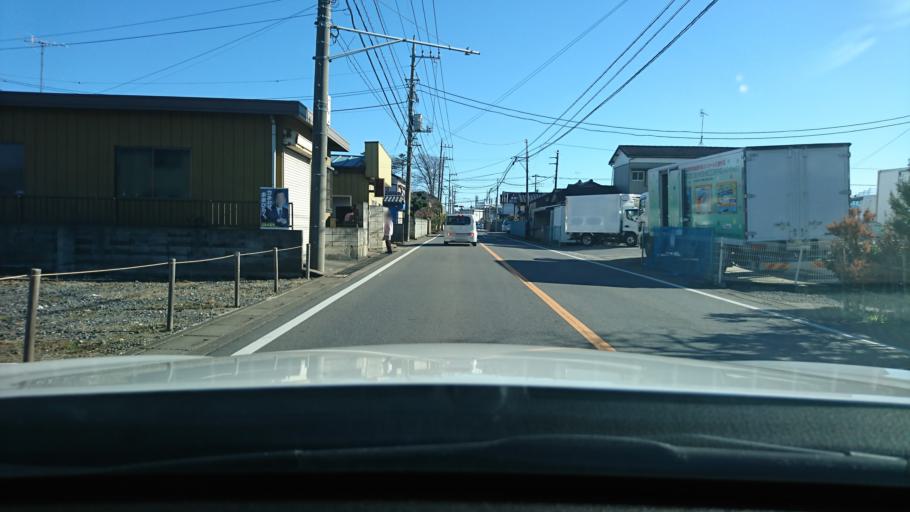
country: JP
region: Saitama
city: Yono
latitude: 35.8971
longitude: 139.5873
